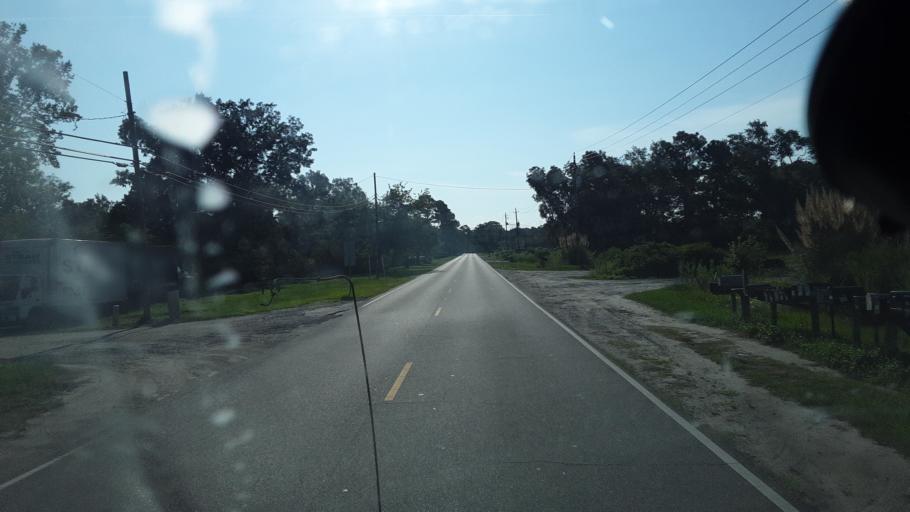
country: US
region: North Carolina
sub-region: Brunswick County
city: Navassa
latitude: 34.2472
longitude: -78.0231
